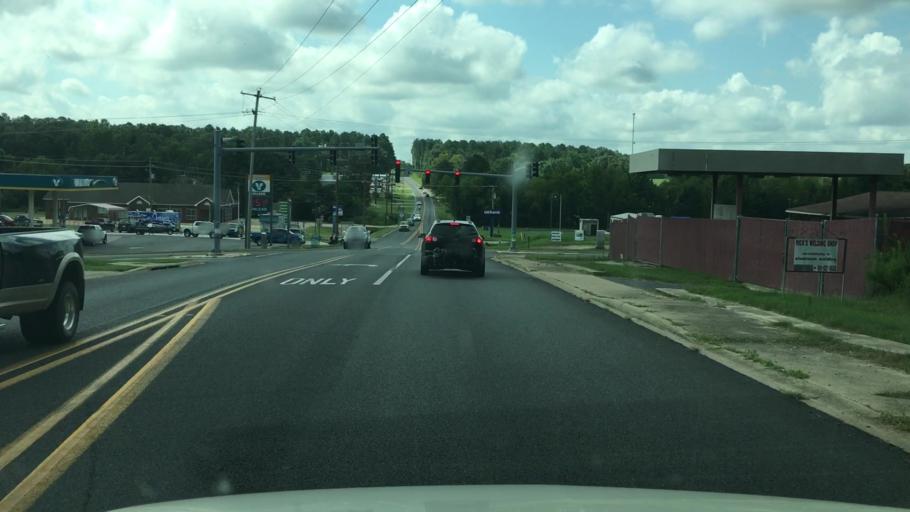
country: US
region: Arkansas
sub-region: Garland County
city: Lake Hamilton
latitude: 34.3169
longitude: -93.1712
